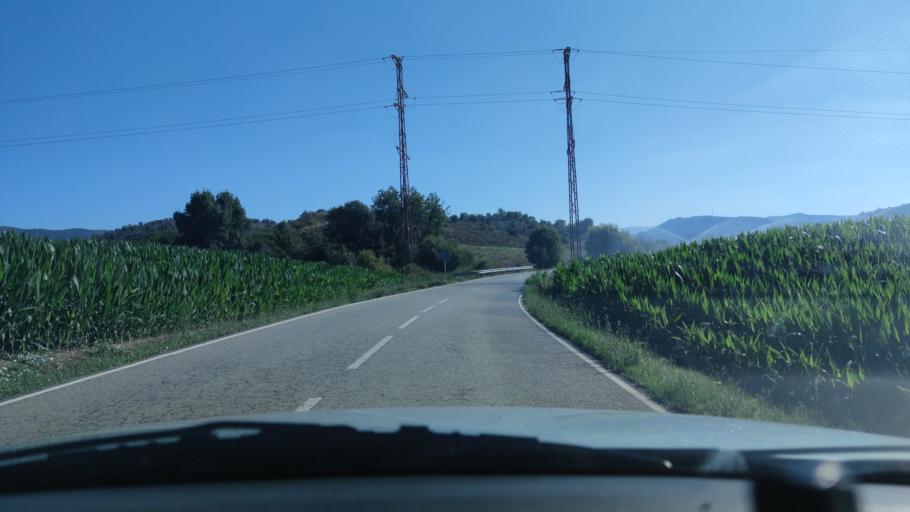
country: ES
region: Catalonia
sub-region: Provincia de Lleida
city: Ponts
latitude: 41.8914
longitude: 1.2322
